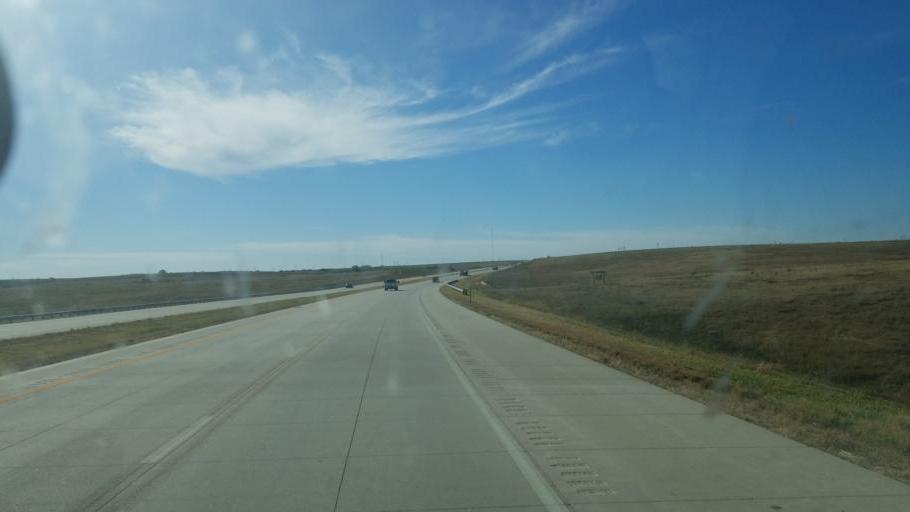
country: US
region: Kansas
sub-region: Ellsworth County
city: Ellsworth
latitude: 38.8494
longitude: -98.1585
